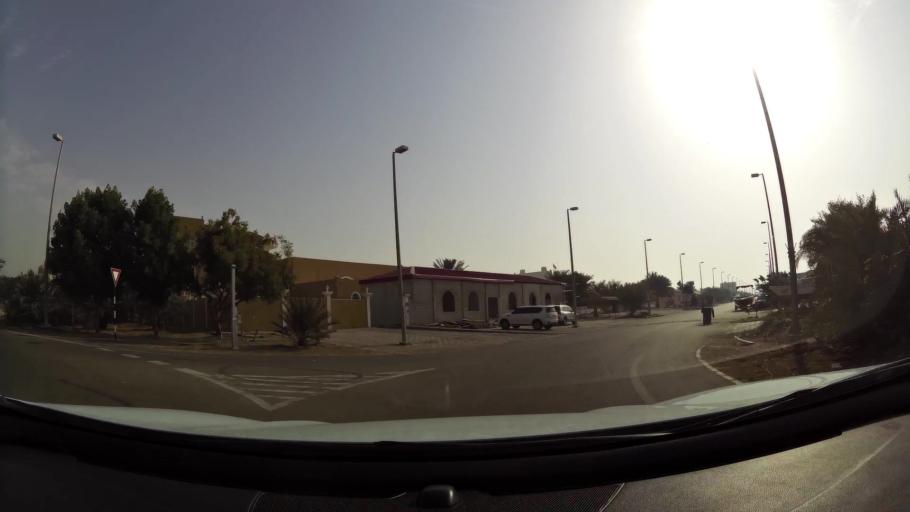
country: AE
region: Abu Dhabi
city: Abu Dhabi
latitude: 24.2624
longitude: 54.6694
